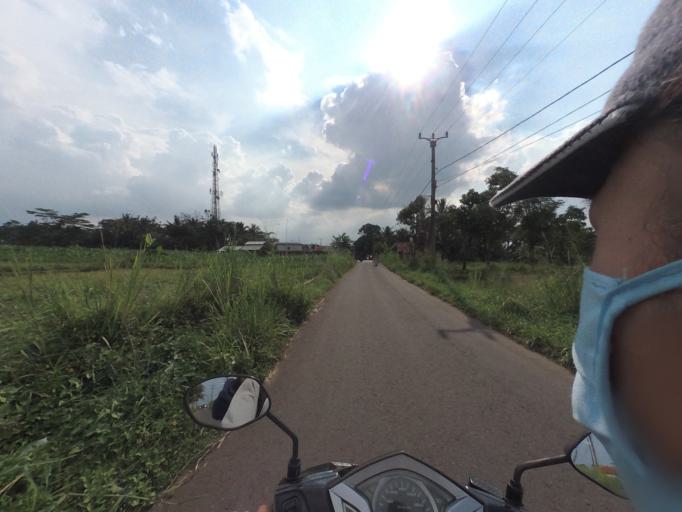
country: ID
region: West Java
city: Ciampea
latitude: -6.6043
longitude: 106.7036
